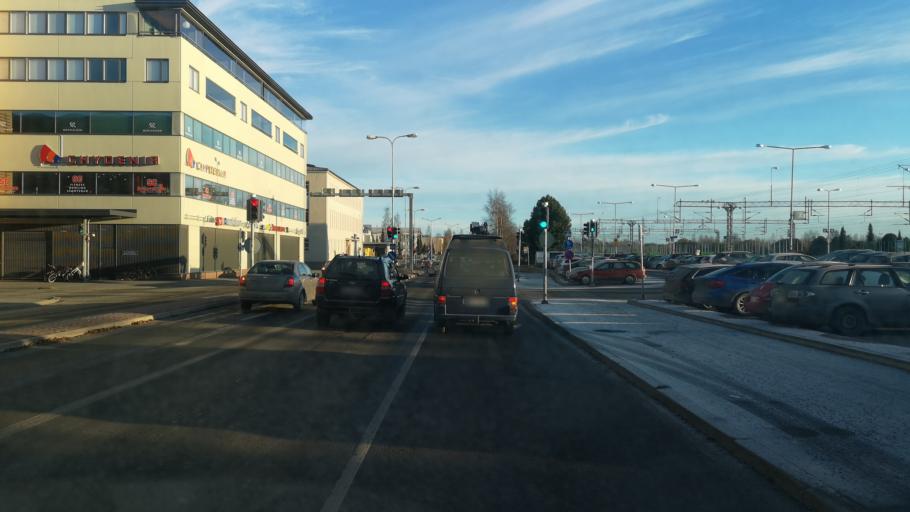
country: FI
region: Central Ostrobothnia
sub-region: Kokkola
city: Kokkola
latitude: 63.8350
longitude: 23.1324
